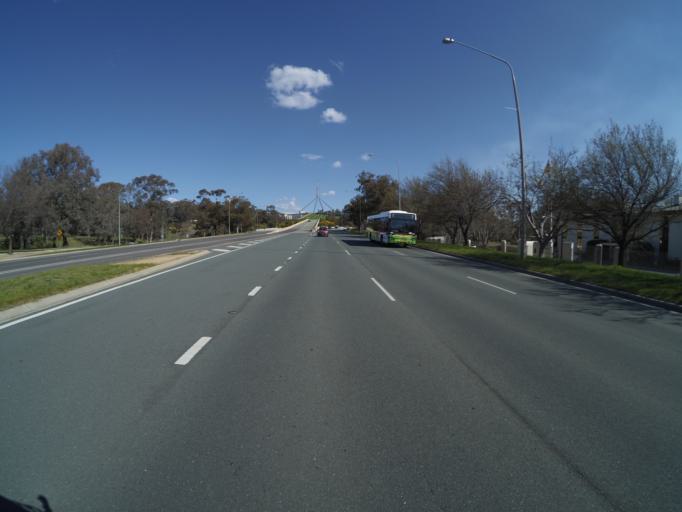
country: AU
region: Australian Capital Territory
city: Forrest
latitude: -35.3026
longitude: 149.1253
